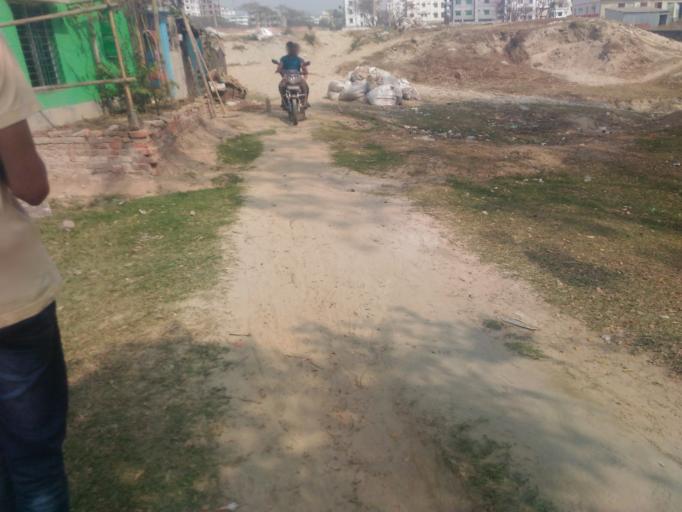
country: BD
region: Dhaka
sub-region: Dhaka
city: Dhaka
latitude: 23.6690
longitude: 90.4223
